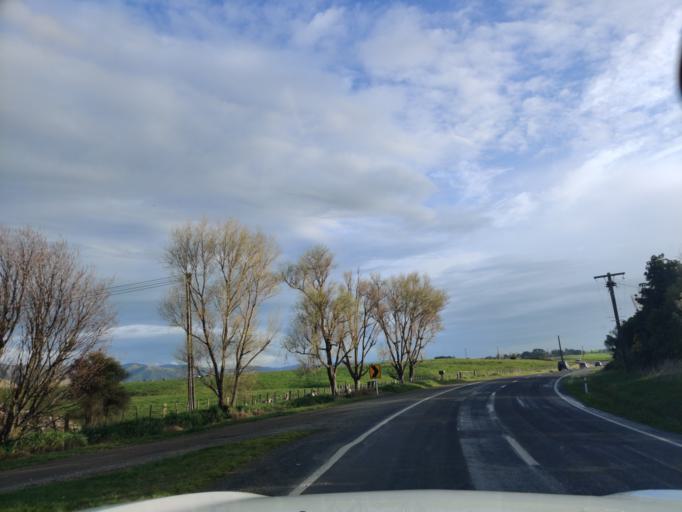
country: NZ
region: Manawatu-Wanganui
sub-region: Palmerston North City
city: Palmerston North
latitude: -40.4973
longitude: 175.4930
